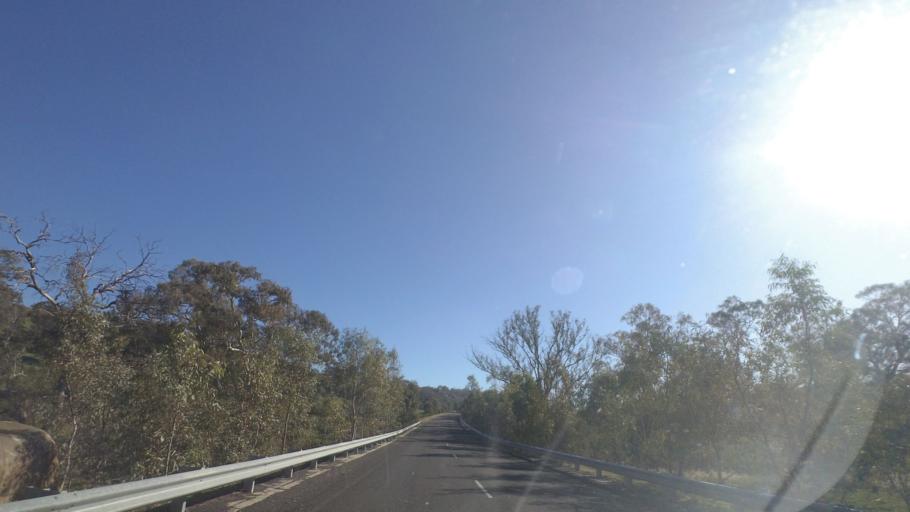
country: AU
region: Victoria
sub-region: Mount Alexander
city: Castlemaine
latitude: -37.0473
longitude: 144.2850
